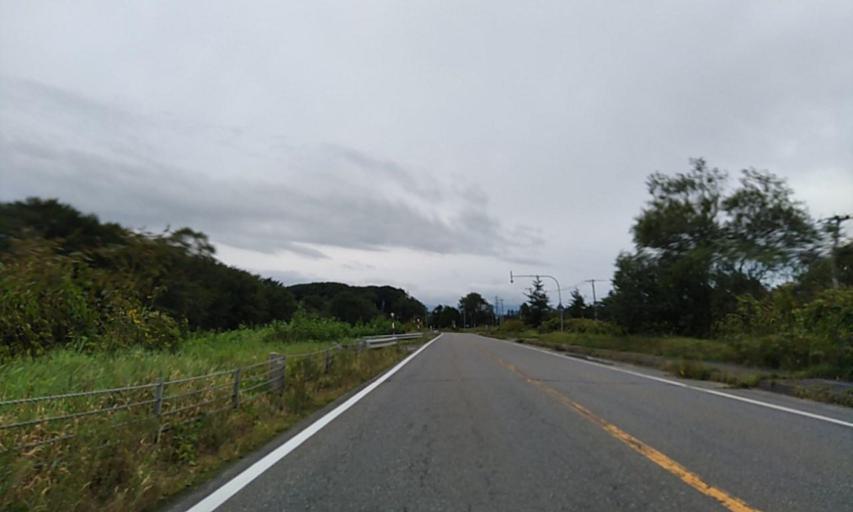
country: JP
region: Hokkaido
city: Obihiro
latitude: 42.4475
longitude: 143.2937
